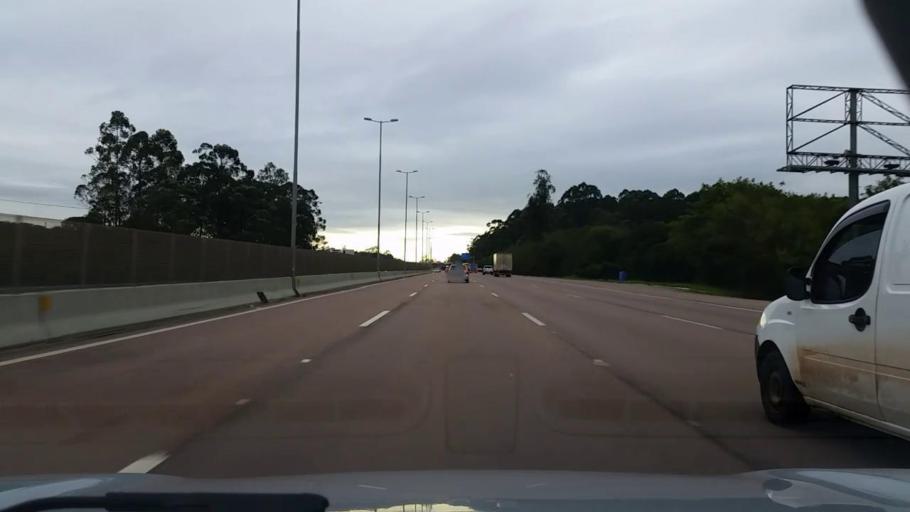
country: BR
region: Rio Grande do Sul
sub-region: Cachoeirinha
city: Cachoeirinha
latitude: -29.9537
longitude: -51.0428
